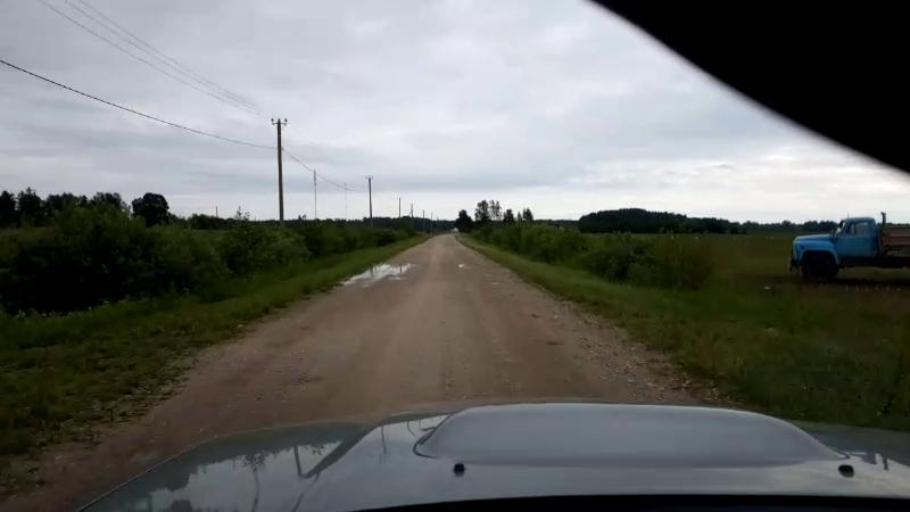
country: EE
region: Paernumaa
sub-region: Halinga vald
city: Parnu-Jaagupi
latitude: 58.5374
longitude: 24.5757
